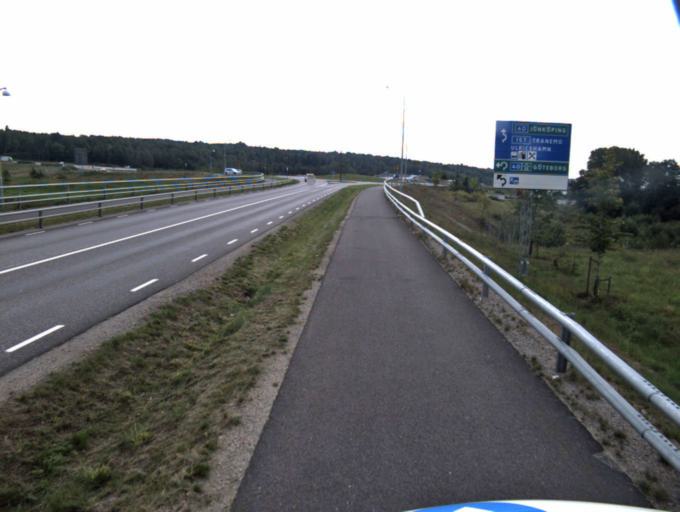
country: SE
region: Vaestra Goetaland
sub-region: Ulricehamns Kommun
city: Ulricehamn
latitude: 57.8115
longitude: 13.4205
